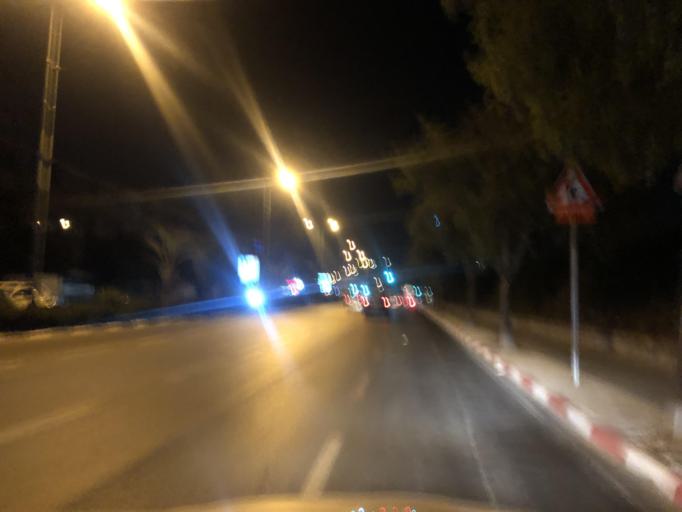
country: IL
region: Tel Aviv
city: Yafo
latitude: 32.0503
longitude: 34.7719
